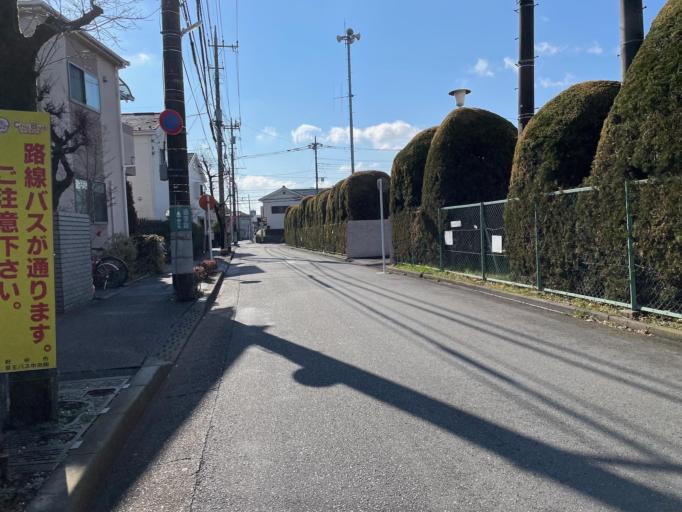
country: JP
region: Tokyo
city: Kokubunji
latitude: 35.6772
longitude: 139.4636
